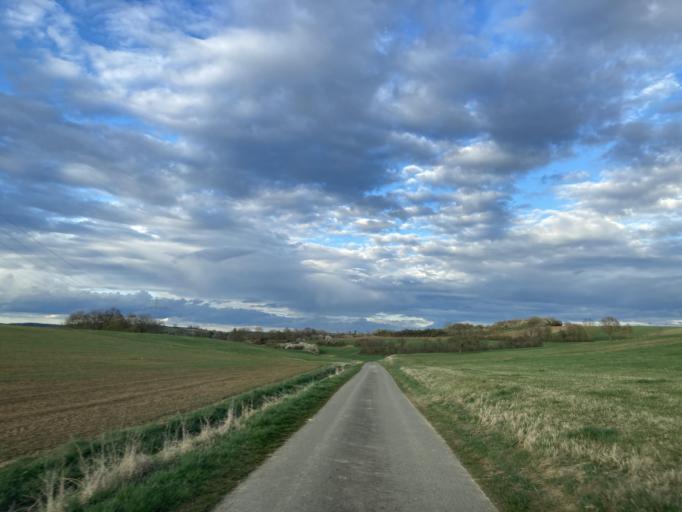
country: DE
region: Baden-Wuerttemberg
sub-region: Tuebingen Region
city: Rottenburg
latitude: 48.4774
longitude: 8.9046
